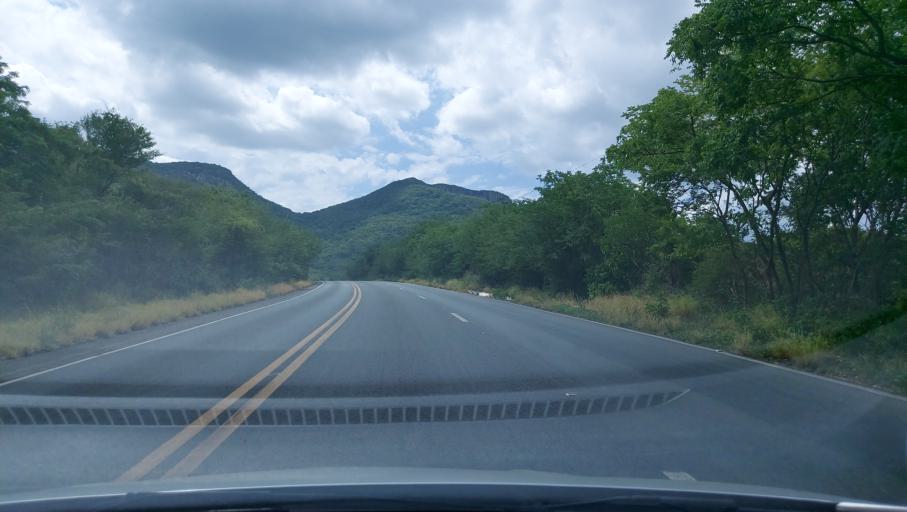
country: BR
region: Bahia
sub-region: Oliveira Dos Brejinhos
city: Beira Rio
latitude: -12.4089
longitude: -42.3734
